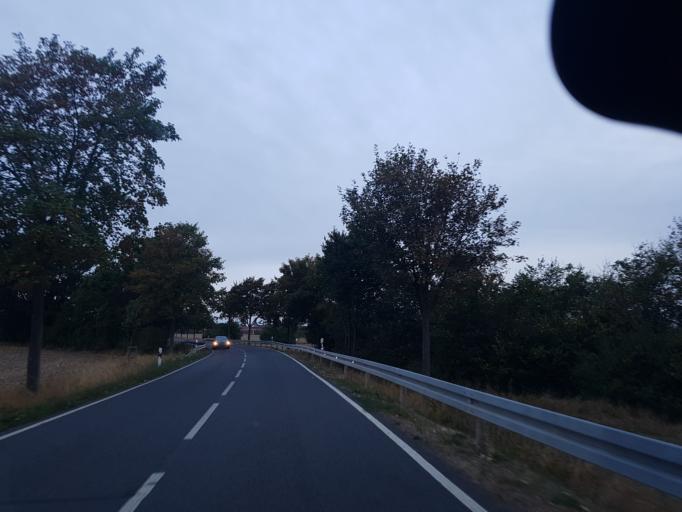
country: DE
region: Brandenburg
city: Muhlberg
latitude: 51.4931
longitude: 13.1955
